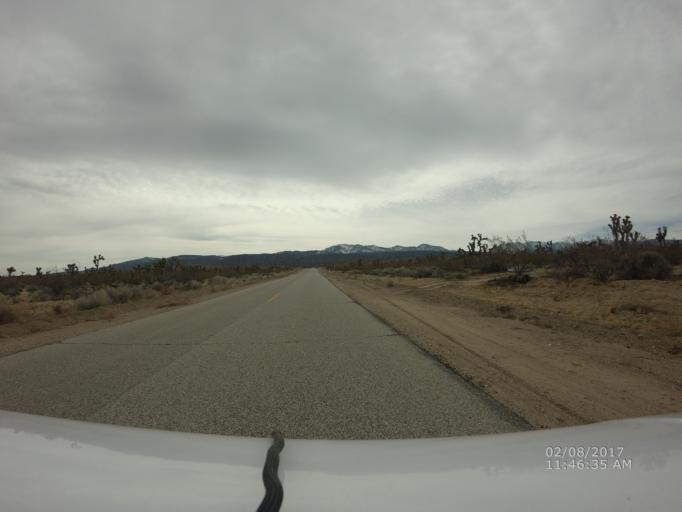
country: US
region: California
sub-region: San Bernardino County
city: Pinon Hills
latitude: 34.4946
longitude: -117.7482
